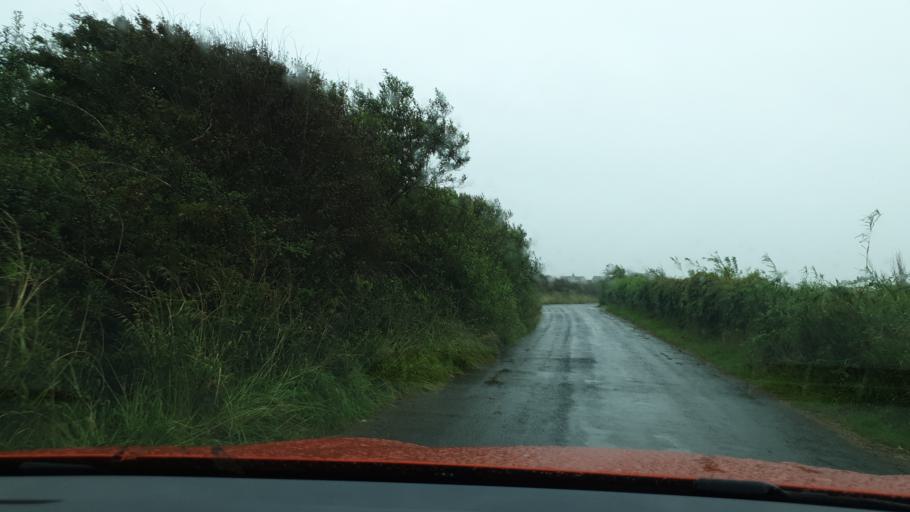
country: GB
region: England
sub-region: Cumbria
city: Barrow in Furness
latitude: 54.1225
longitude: -3.2599
